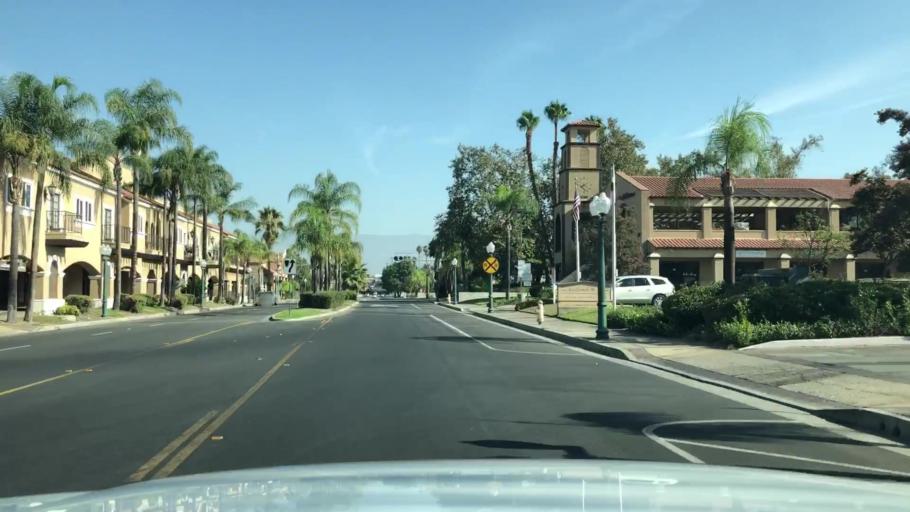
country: US
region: California
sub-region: San Bernardino County
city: Redlands
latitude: 34.0578
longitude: -117.1803
